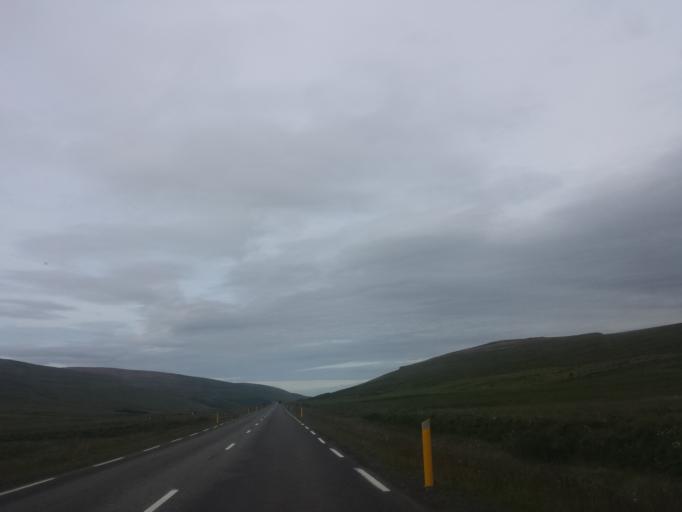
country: IS
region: Northeast
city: Laugar
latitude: 65.7602
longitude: -17.5830
